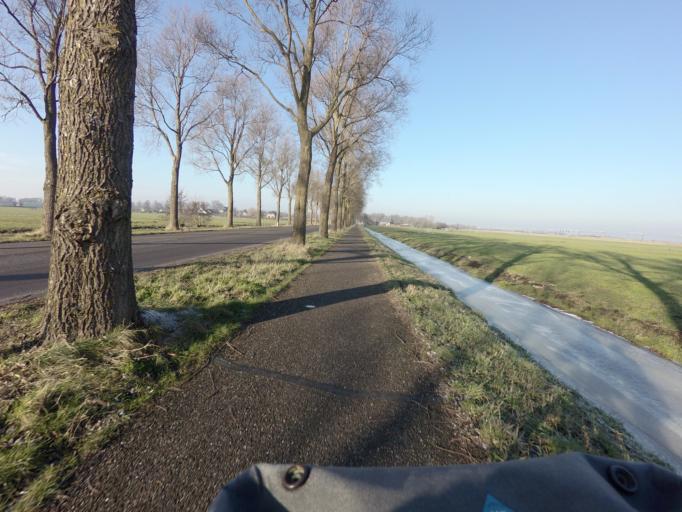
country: NL
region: North Holland
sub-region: Gemeente Amsterdam
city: Amsterdam-Zuidoost
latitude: 52.2641
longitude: 4.9842
